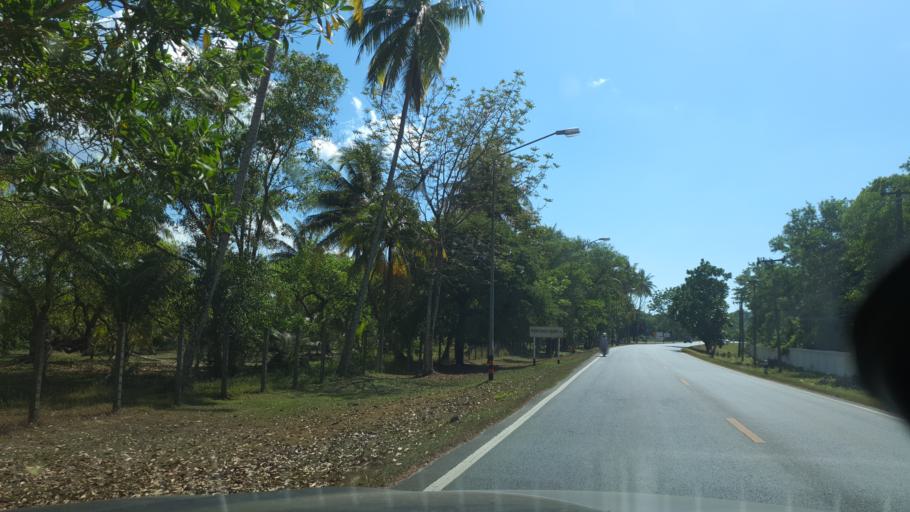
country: TH
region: Phangnga
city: Ban Khao Lak
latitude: 8.5844
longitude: 98.2477
